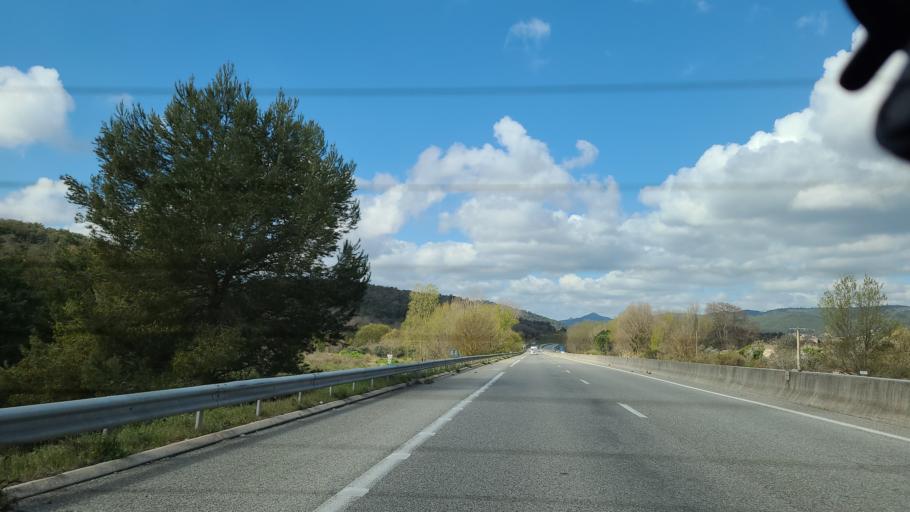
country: FR
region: Provence-Alpes-Cote d'Azur
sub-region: Departement du Var
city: Pignans
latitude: 43.2895
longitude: 6.2181
